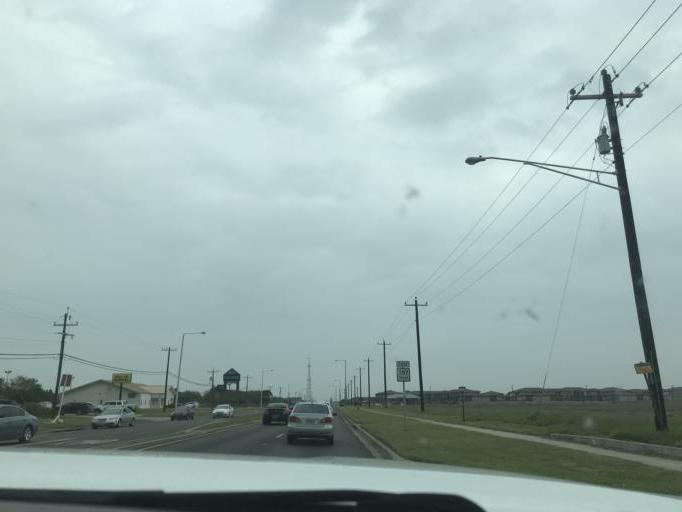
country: US
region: Texas
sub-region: Nueces County
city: Corpus Christi
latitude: 27.6755
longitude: -97.3637
